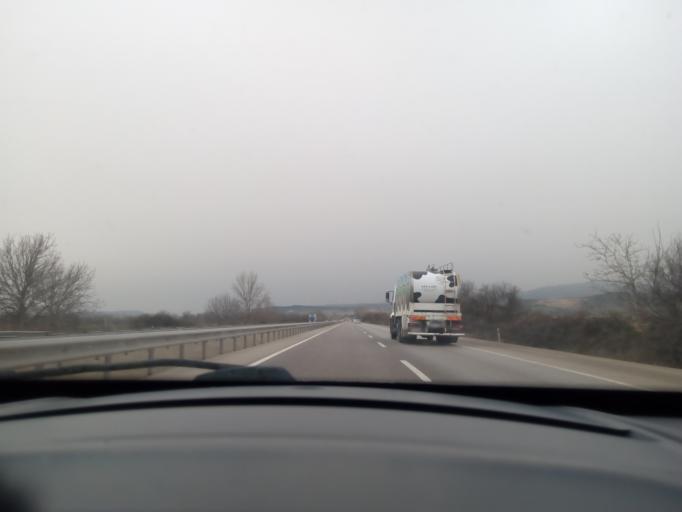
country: TR
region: Balikesir
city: Gobel
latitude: 39.9849
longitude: 28.1942
